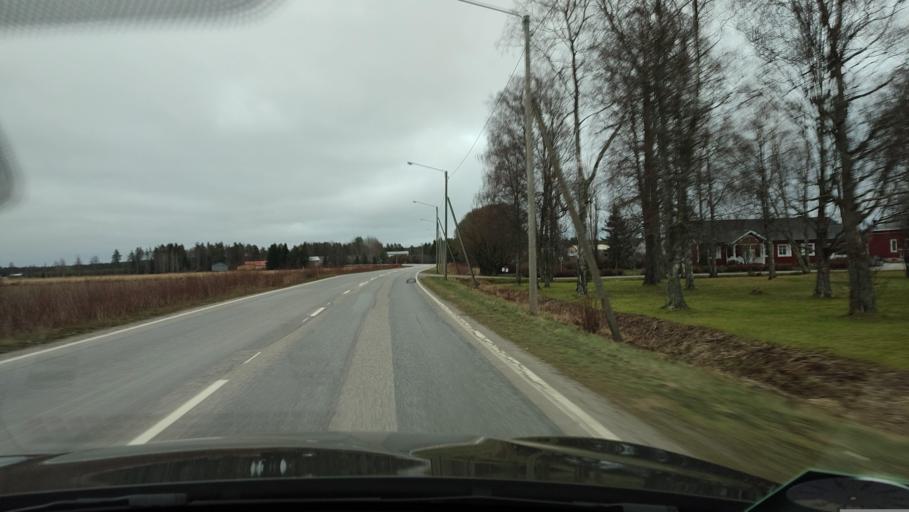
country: FI
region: Southern Ostrobothnia
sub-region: Suupohja
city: Karijoki
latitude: 62.2356
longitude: 21.6723
